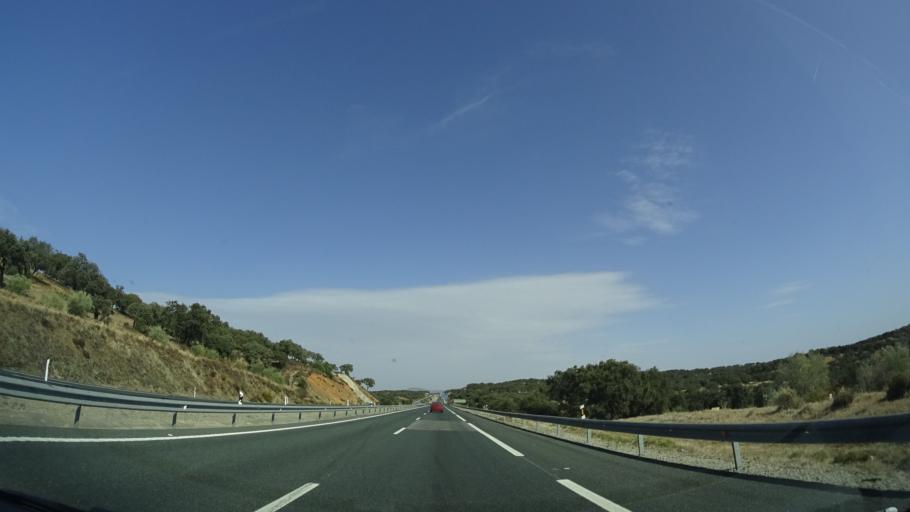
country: ES
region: Andalusia
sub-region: Provincia de Huelva
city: Santa Olalla del Cala
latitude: 37.8819
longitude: -6.2198
